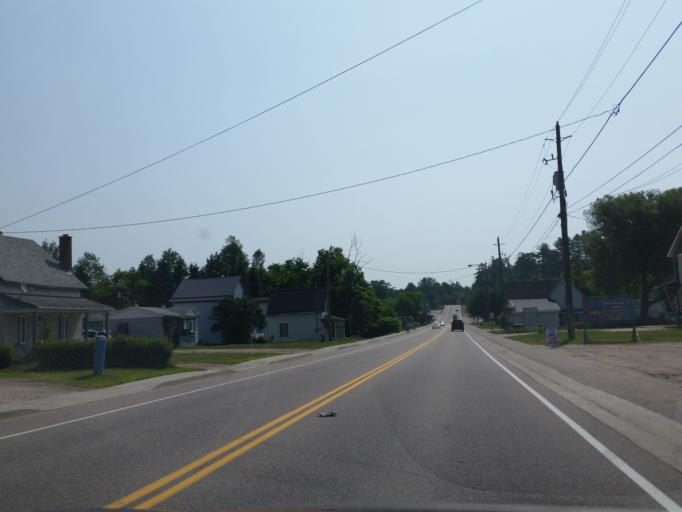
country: CA
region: Ontario
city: Mattawa
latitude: 46.3167
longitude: -78.6980
